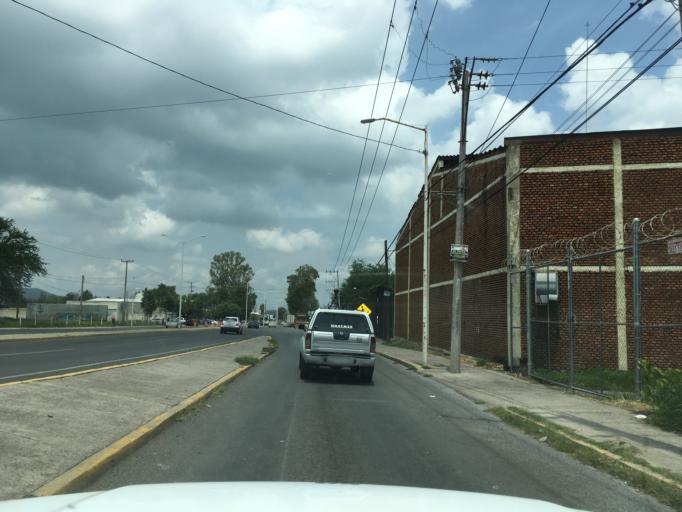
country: MX
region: Jalisco
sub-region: Tlajomulco de Zuniga
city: Santa Cruz de las Flores
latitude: 20.4895
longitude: -103.4929
